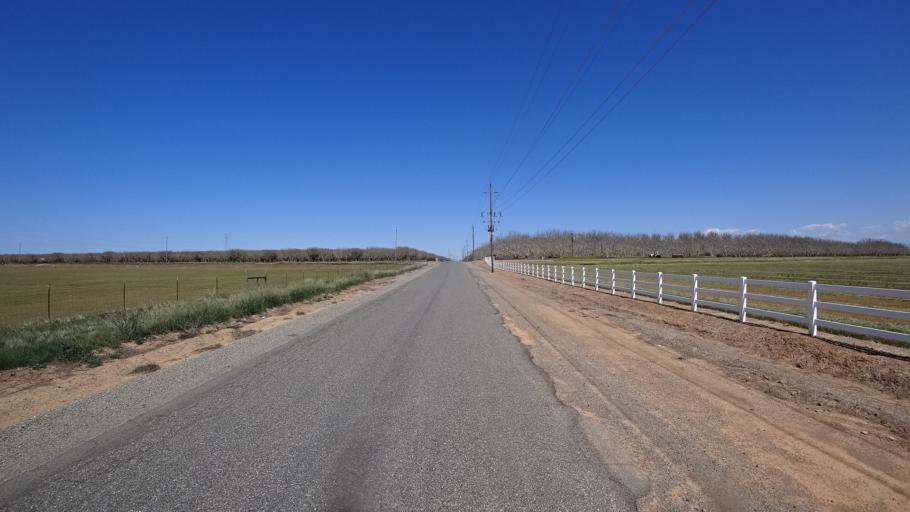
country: US
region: California
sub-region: Glenn County
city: Orland
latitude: 39.7783
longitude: -122.1409
